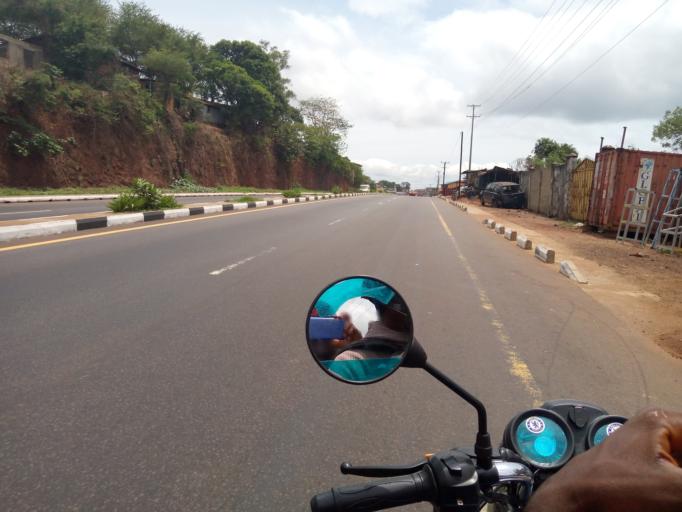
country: SL
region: Western Area
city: Hastings
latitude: 8.4213
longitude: -13.1556
